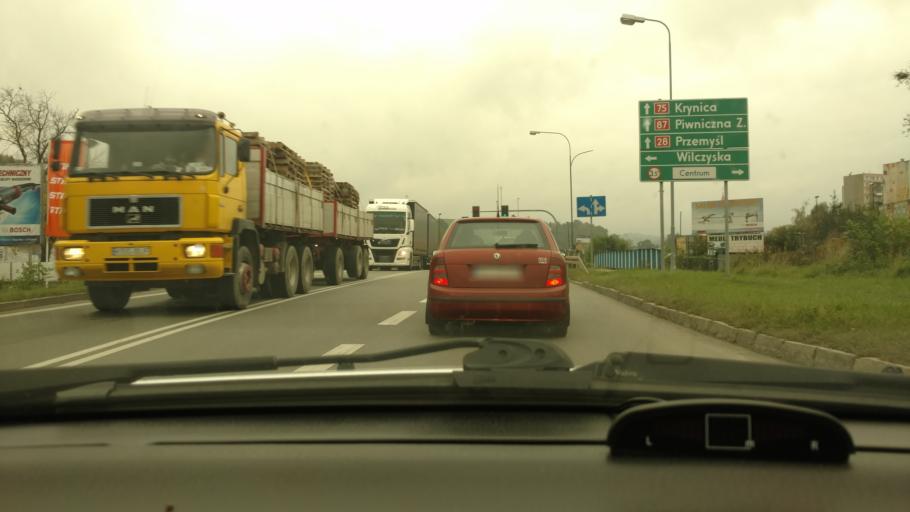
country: PL
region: Lesser Poland Voivodeship
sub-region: Powiat nowosadecki
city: Nowy Sacz
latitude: 49.6333
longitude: 20.7107
